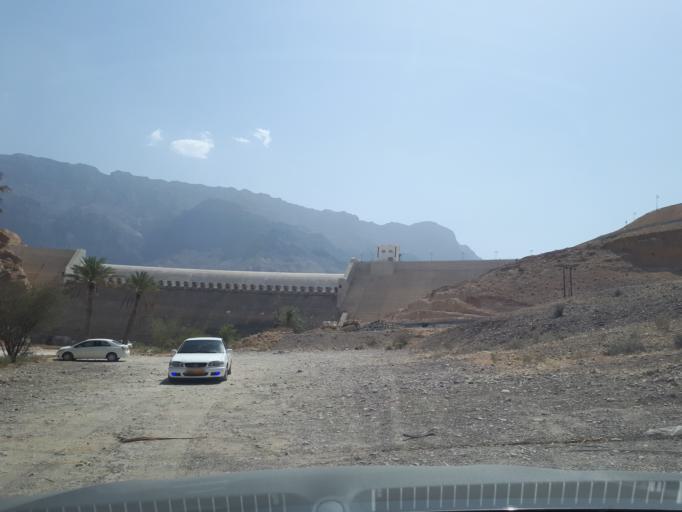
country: OM
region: Ash Sharqiyah
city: Ibra'
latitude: 23.0849
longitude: 58.8512
